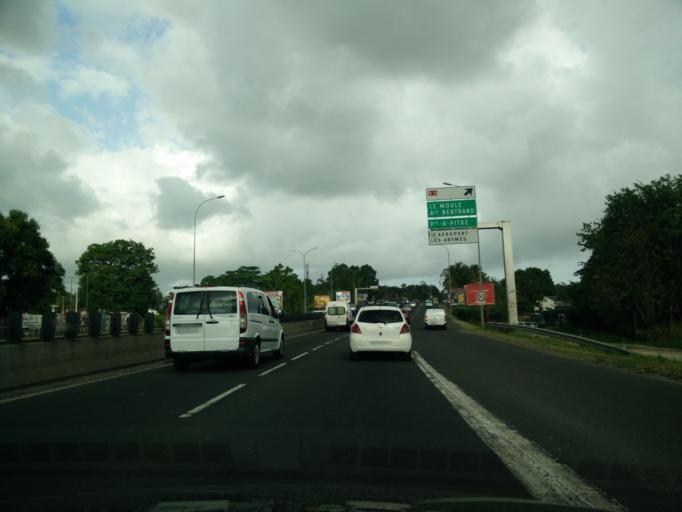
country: GP
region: Guadeloupe
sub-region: Guadeloupe
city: Pointe-a-Pitre
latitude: 16.2520
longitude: -61.5315
